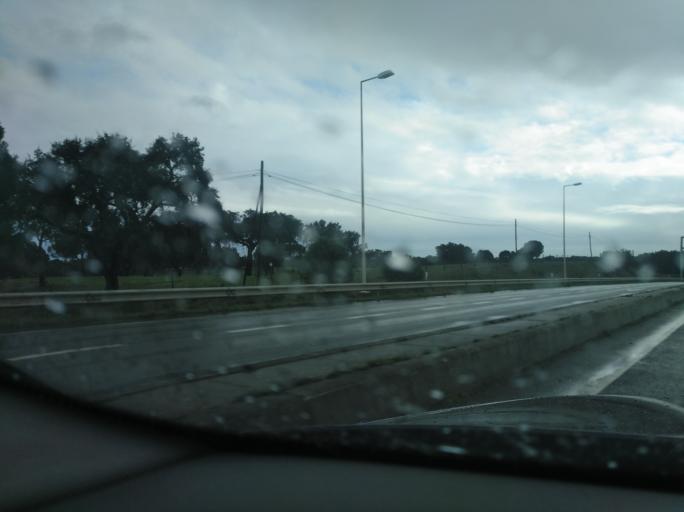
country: PT
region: Setubal
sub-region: Grandola
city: Grandola
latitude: 38.1103
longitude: -8.4183
